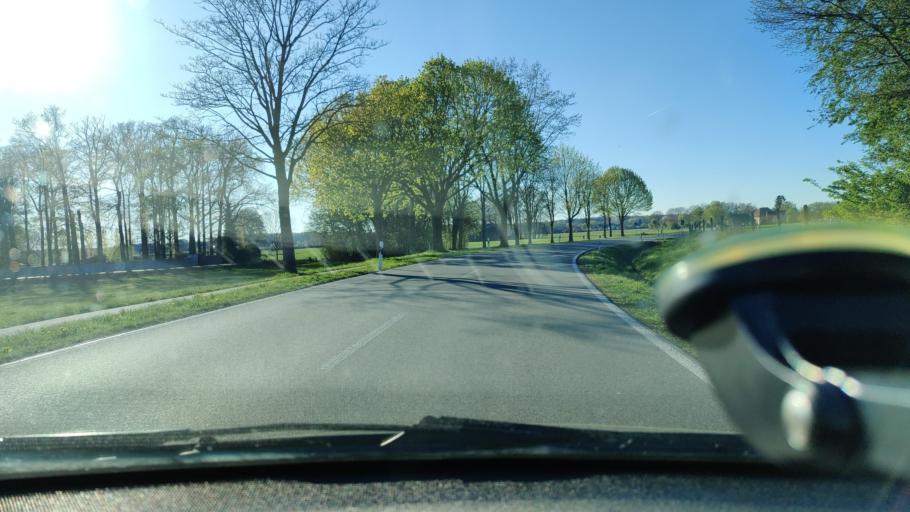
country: DE
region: North Rhine-Westphalia
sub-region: Regierungsbezirk Munster
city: Legden
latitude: 52.0239
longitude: 7.1076
